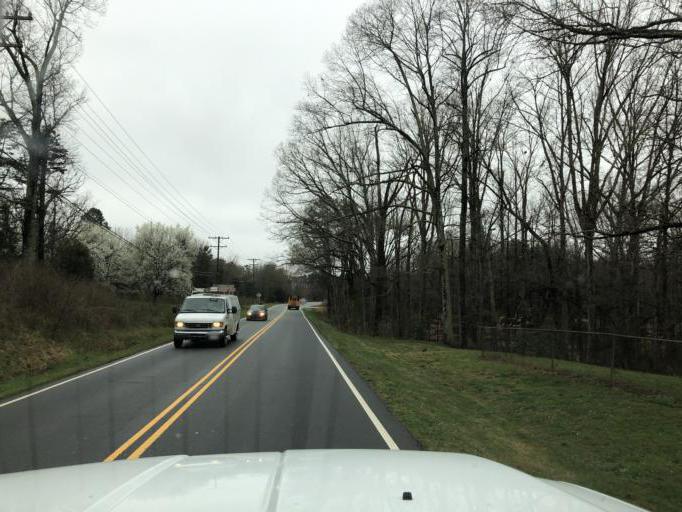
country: US
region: North Carolina
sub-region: Mecklenburg County
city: Huntersville
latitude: 35.3389
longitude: -80.9110
